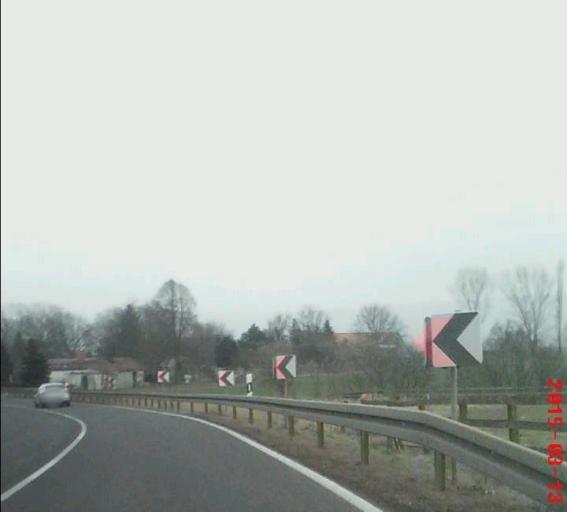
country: DE
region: Thuringia
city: Dollstadt
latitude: 51.0807
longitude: 10.8082
